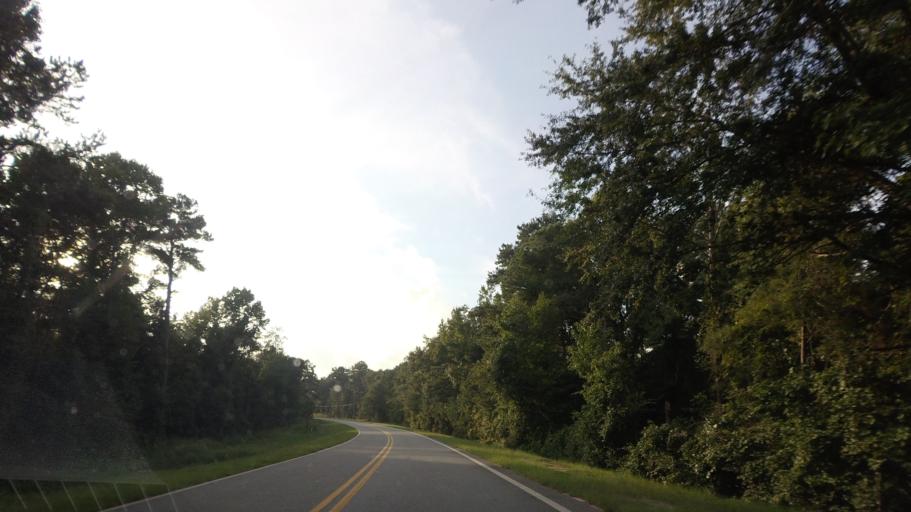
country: US
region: Georgia
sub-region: Wilkinson County
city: Gordon
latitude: 32.8230
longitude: -83.4066
